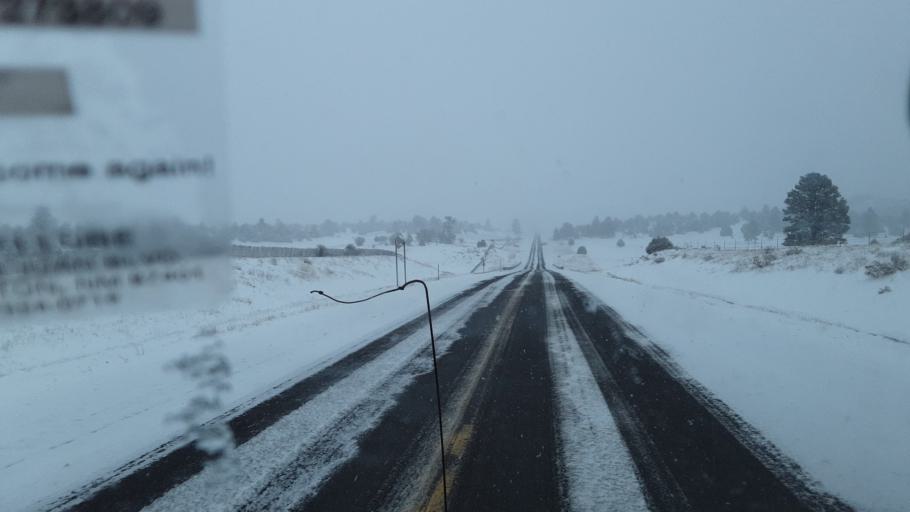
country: US
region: New Mexico
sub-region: Rio Arriba County
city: Dulce
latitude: 36.9315
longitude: -106.7969
